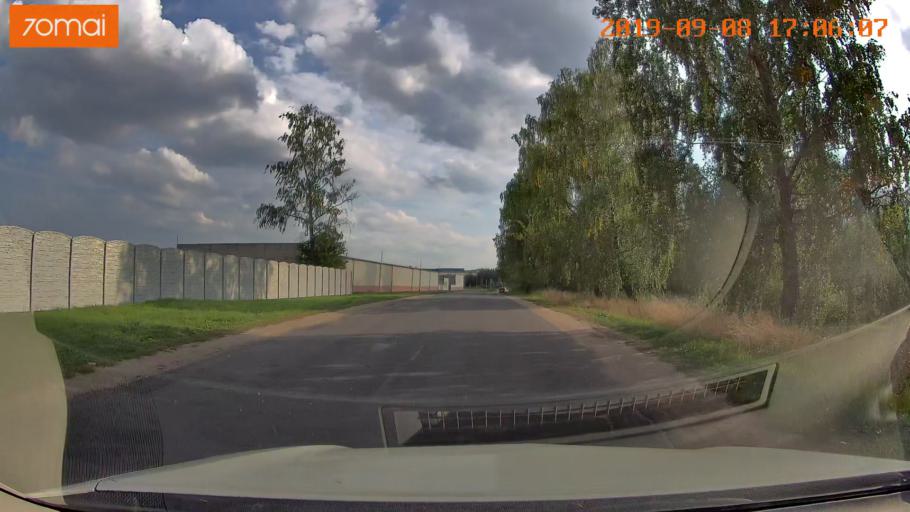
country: BY
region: Grodnenskaya
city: Hrodna
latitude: 53.6732
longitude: 23.9533
